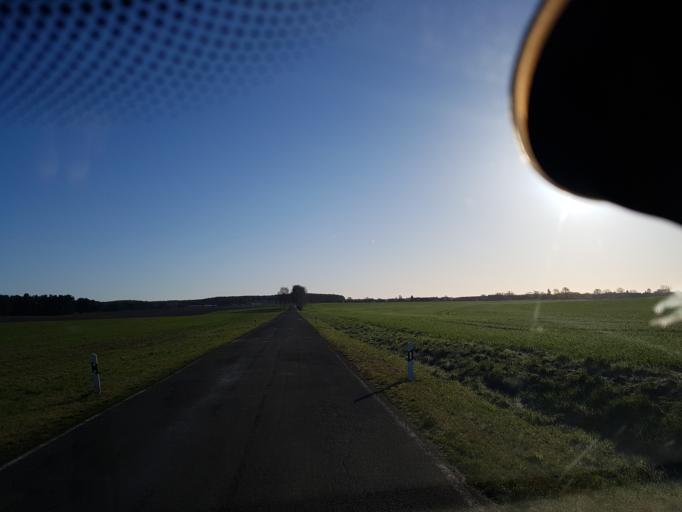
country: DE
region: Brandenburg
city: Jamlitz
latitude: 52.0438
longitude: 14.4057
